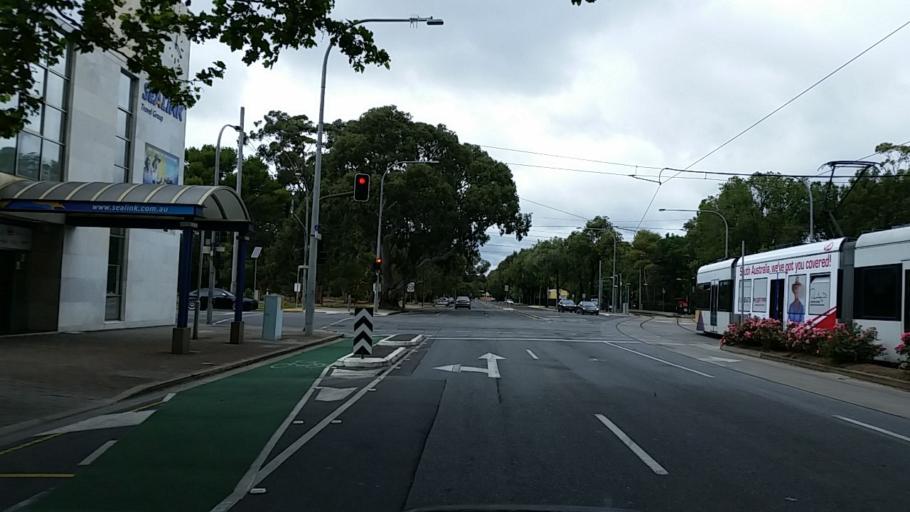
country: AU
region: South Australia
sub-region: Adelaide
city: Adelaide
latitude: -34.9353
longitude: 138.6005
